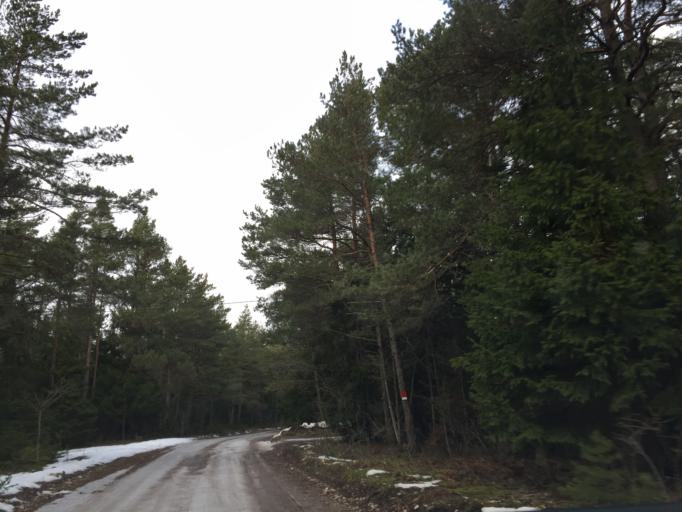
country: EE
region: Saare
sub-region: Kuressaare linn
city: Kuressaare
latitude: 58.4916
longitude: 21.9344
